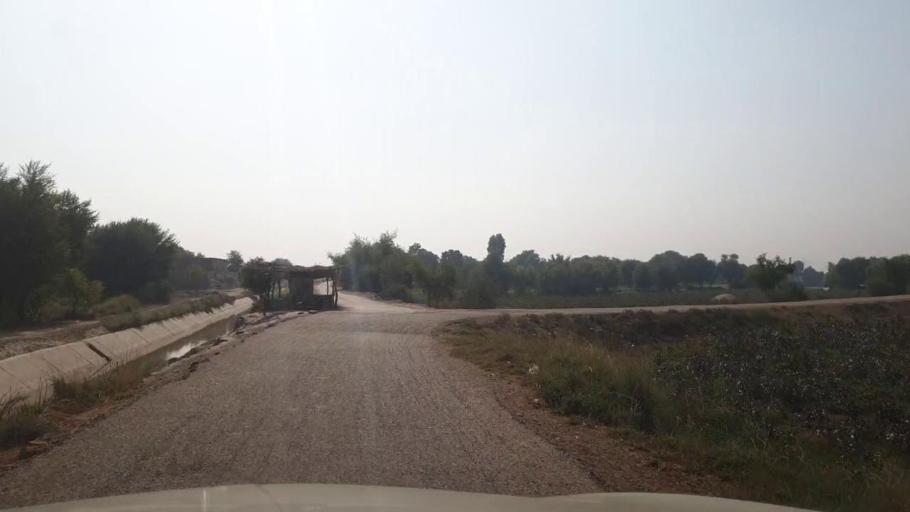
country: PK
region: Sindh
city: Bhan
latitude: 26.5188
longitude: 67.7800
